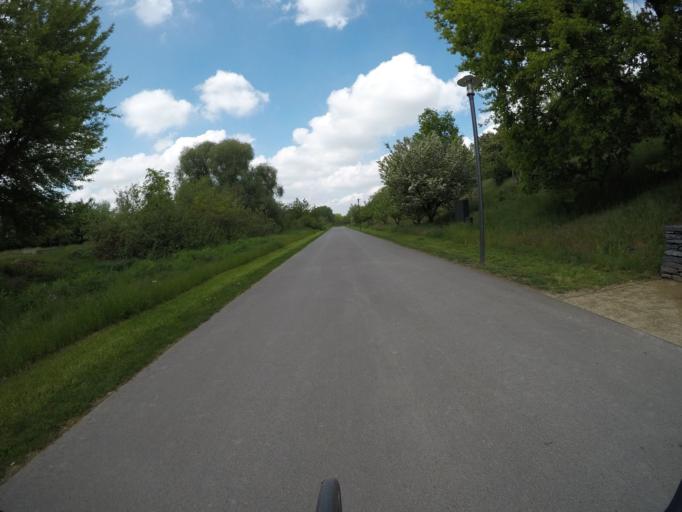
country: DE
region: Berlin
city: Kaulsdorf
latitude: 52.5312
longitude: 13.5812
